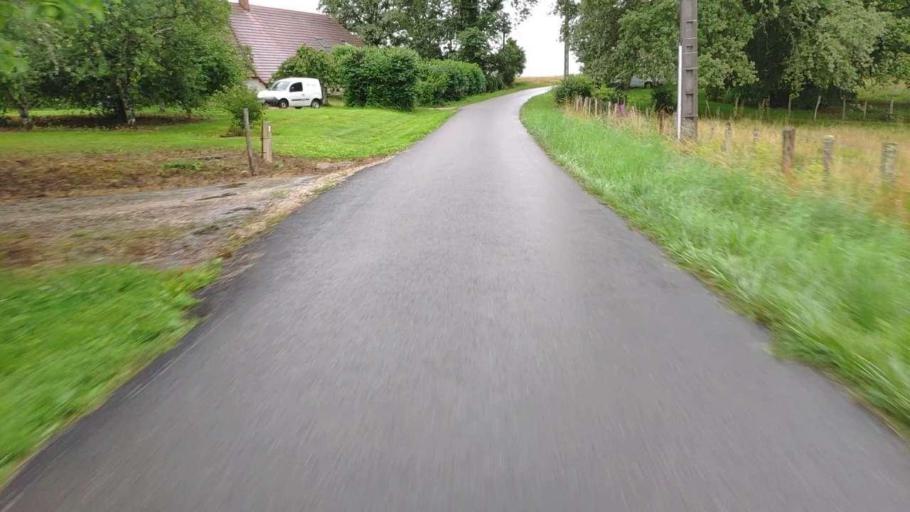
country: FR
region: Franche-Comte
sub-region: Departement du Jura
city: Chaussin
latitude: 46.8794
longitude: 5.4150
